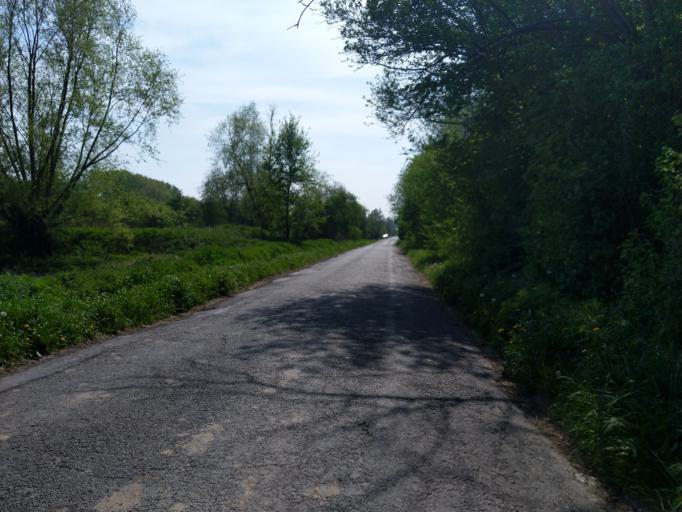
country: BE
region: Wallonia
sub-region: Province du Hainaut
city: Mons
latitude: 50.4475
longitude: 4.0265
